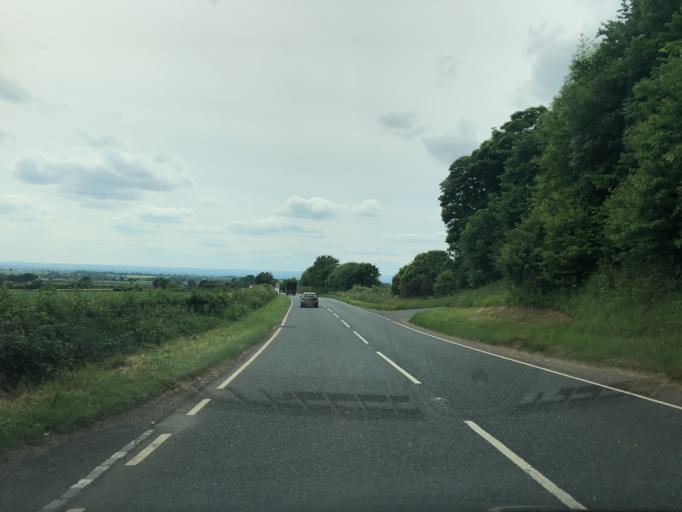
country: GB
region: England
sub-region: North Yorkshire
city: Angram Grange
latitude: 54.2357
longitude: -1.2338
